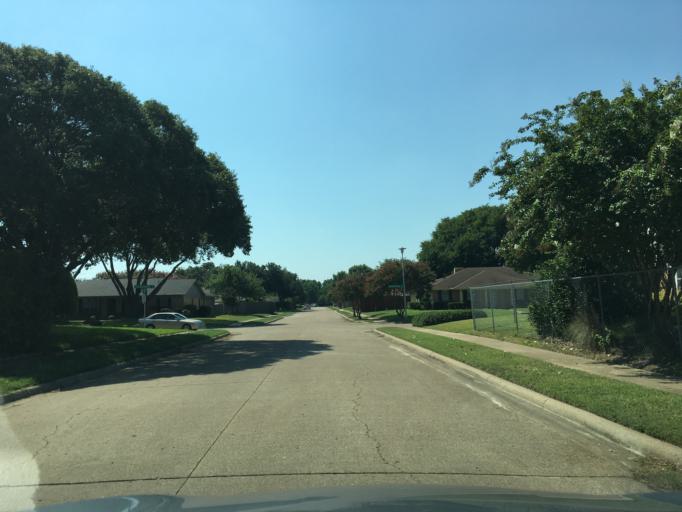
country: US
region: Texas
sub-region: Dallas County
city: Garland
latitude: 32.9369
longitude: -96.6526
